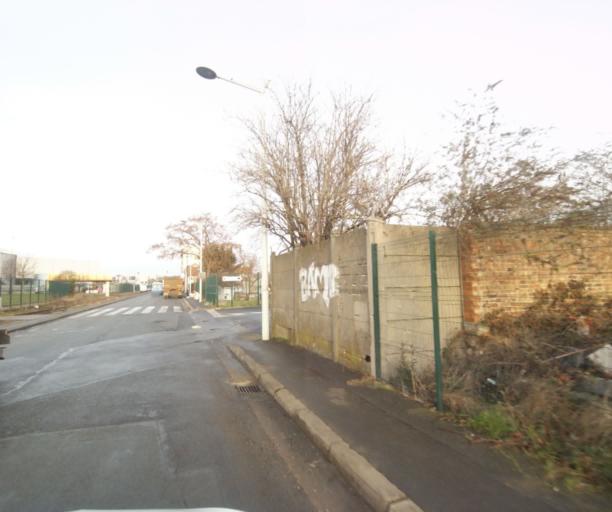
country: FR
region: Ile-de-France
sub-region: Departement des Yvelines
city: Carrieres-sur-Seine
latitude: 48.8977
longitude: 2.1859
